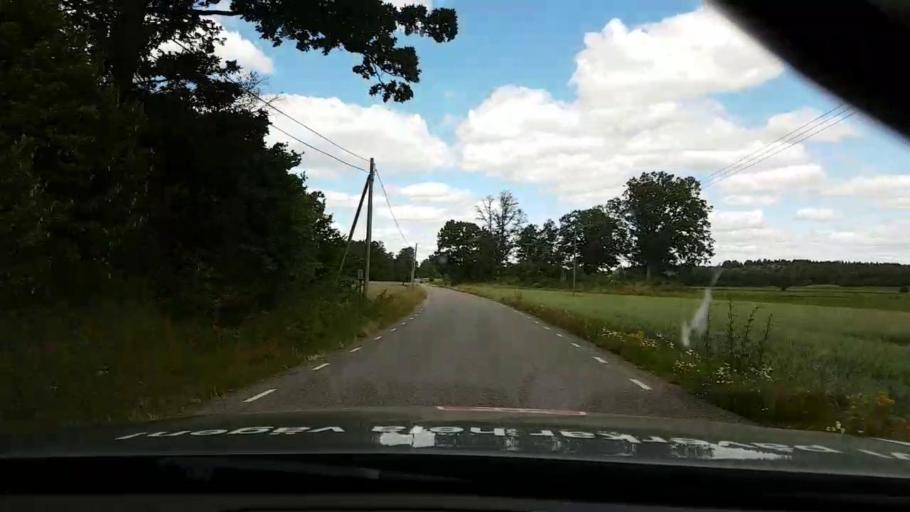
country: SE
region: Kalmar
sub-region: Vasterviks Kommun
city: Forserum
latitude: 57.9895
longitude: 16.6049
